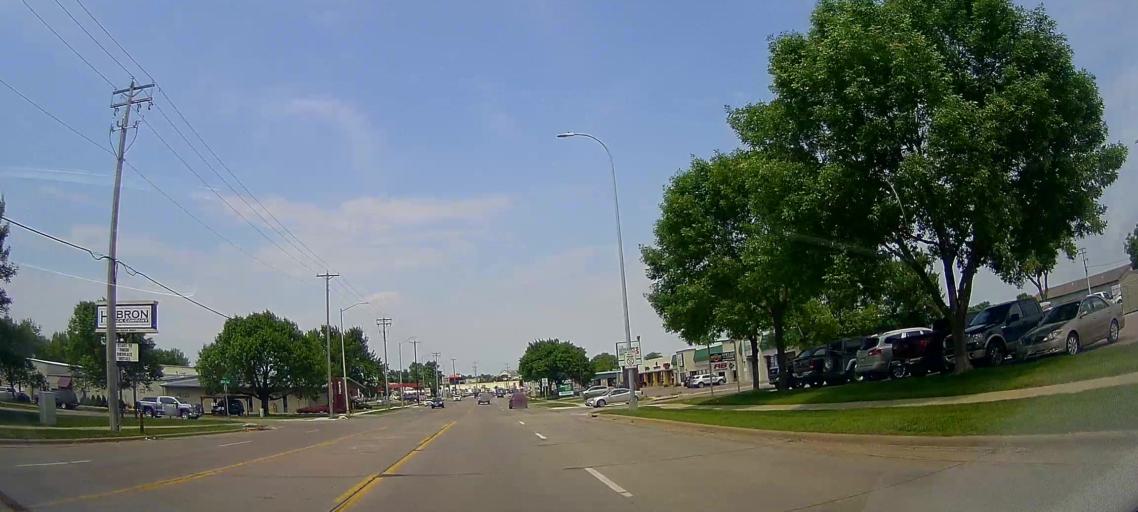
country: US
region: South Dakota
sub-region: Minnehaha County
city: Sioux Falls
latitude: 43.5063
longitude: -96.7502
